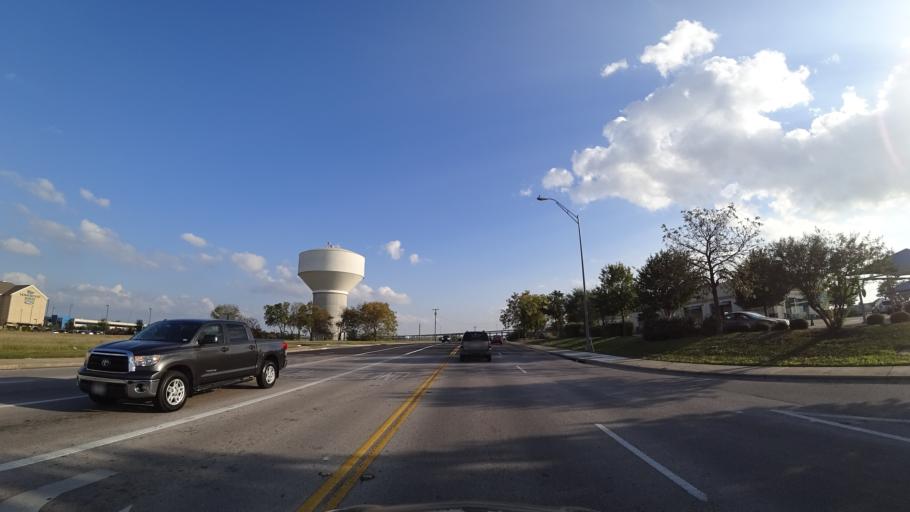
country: US
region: Texas
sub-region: Williamson County
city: Round Rock
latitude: 30.4897
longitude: -97.6747
